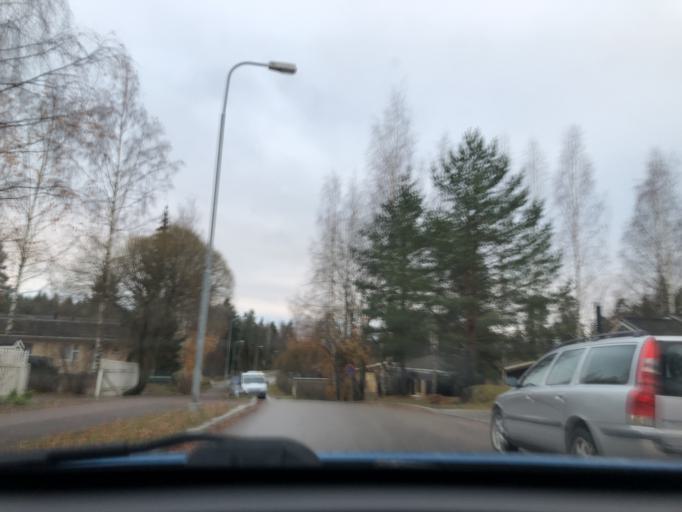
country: FI
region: Pirkanmaa
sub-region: Tampere
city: Kangasala
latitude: 61.5271
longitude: 23.9525
